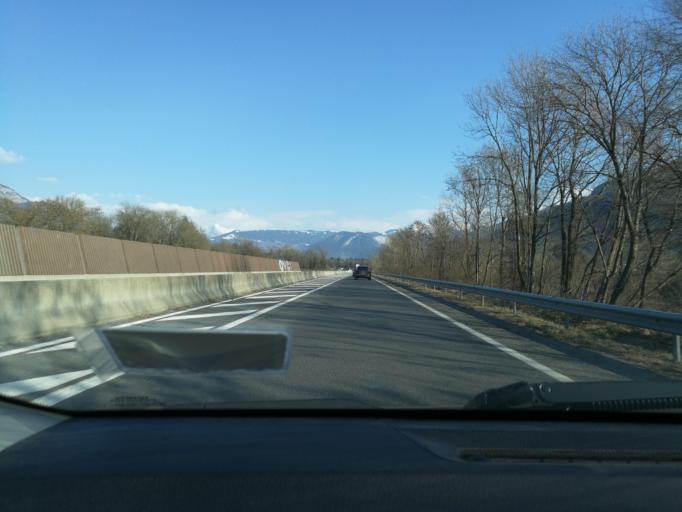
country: FR
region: Rhone-Alpes
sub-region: Departement de la Haute-Savoie
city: Vougy
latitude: 46.0722
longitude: 6.4714
